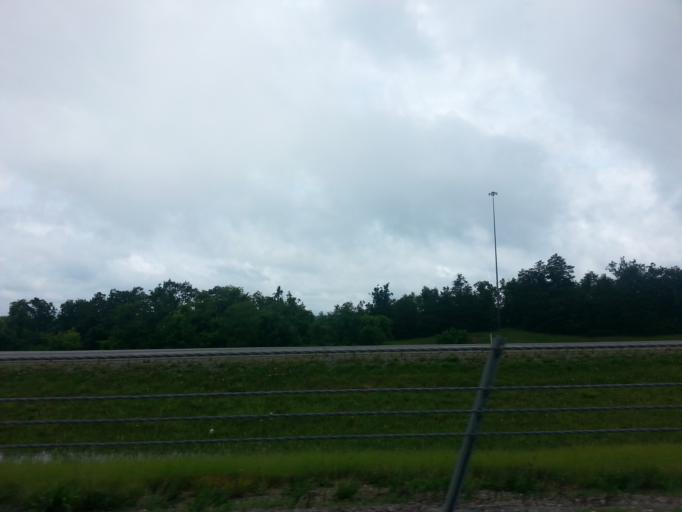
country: US
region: Tennessee
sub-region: Putnam County
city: Monterey
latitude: 36.1399
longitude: -85.2800
